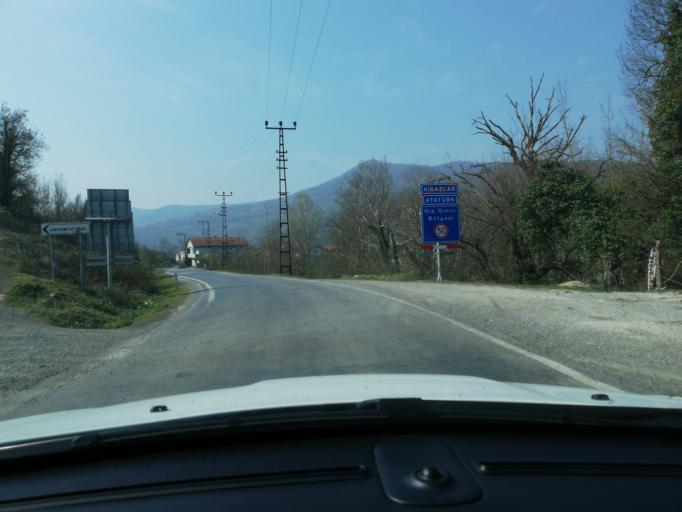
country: TR
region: Karabuk
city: Yenice
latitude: 41.2564
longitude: 32.3603
